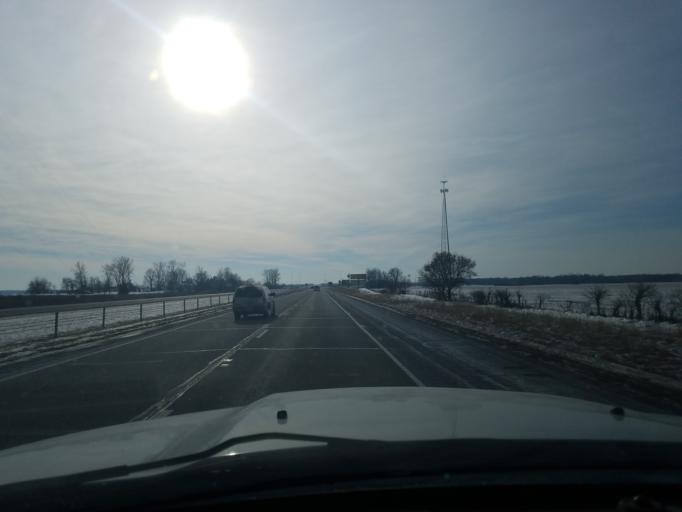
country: US
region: Indiana
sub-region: Huntington County
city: Warren
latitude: 40.7285
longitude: -85.4263
